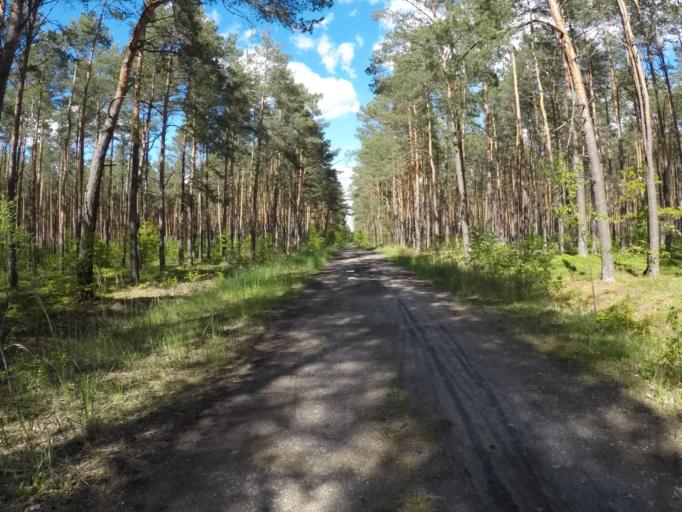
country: PL
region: Swietokrzyskie
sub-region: Powiat kielecki
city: Kostomloty Drugie
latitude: 50.8916
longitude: 20.5406
